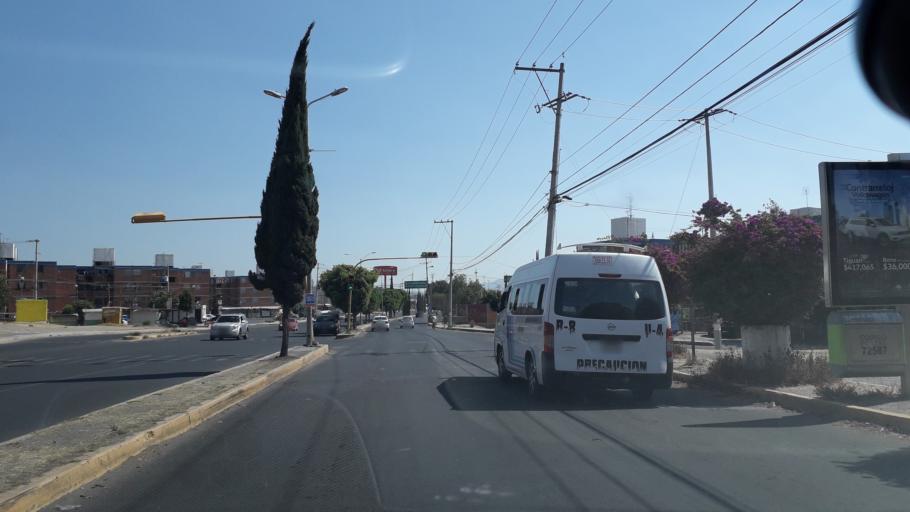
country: MX
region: Puebla
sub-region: Puebla
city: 18 de Marzo
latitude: 18.9846
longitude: -98.2172
